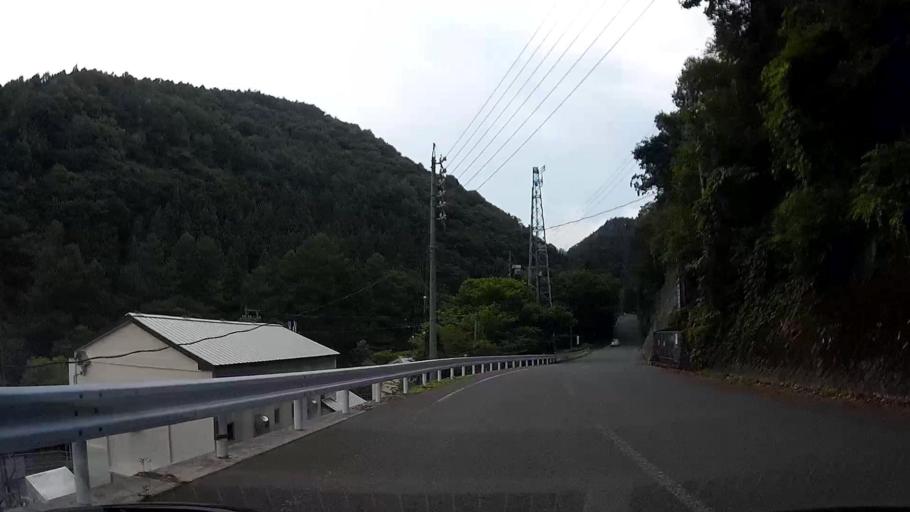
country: JP
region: Nagano
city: Iiyama
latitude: 36.8267
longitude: 138.4236
